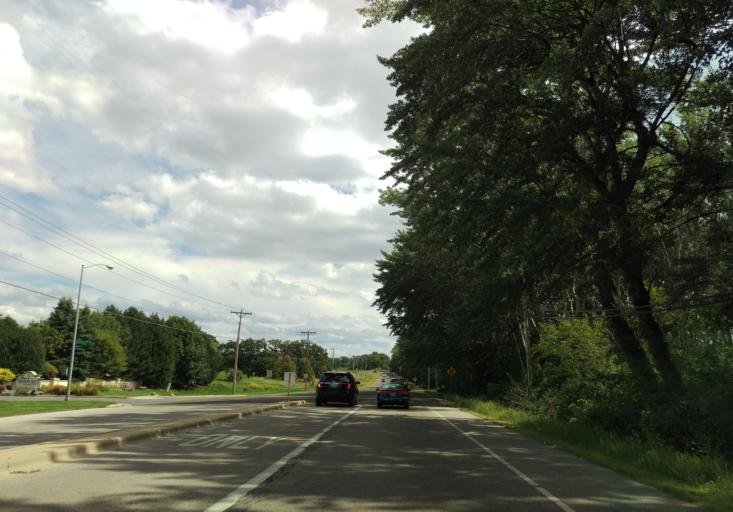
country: US
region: Wisconsin
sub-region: Dane County
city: Shorewood Hills
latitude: 43.1119
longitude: -89.4652
